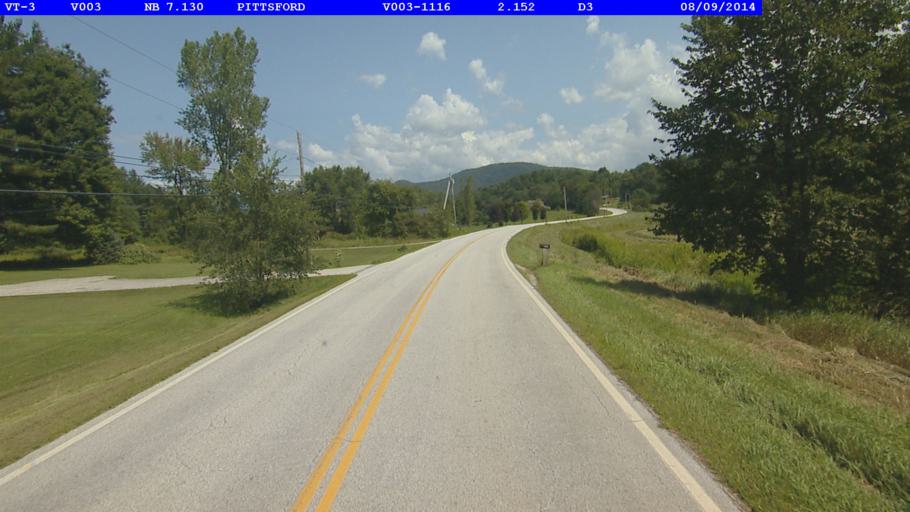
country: US
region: Vermont
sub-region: Rutland County
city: Rutland
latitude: 43.6928
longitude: -73.0159
